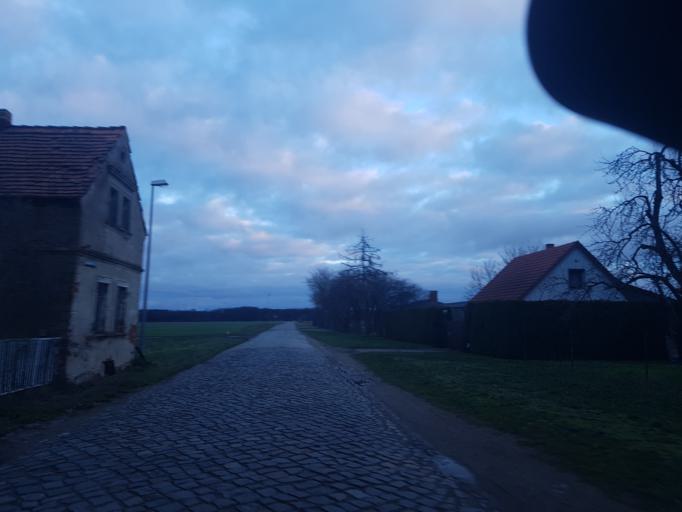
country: DE
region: Brandenburg
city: Muhlberg
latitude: 51.4757
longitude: 13.2081
